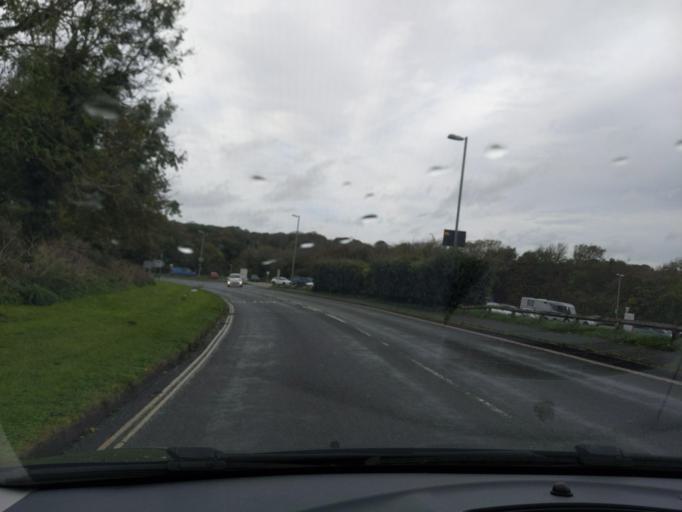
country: GB
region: England
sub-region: Cornwall
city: Padstow
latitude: 50.5392
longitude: -4.9415
